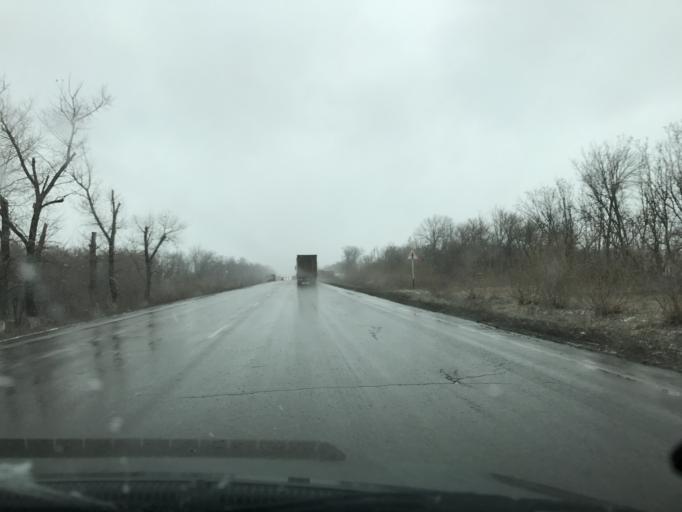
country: RU
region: Rostov
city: Bataysk
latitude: 47.0664
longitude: 39.8046
